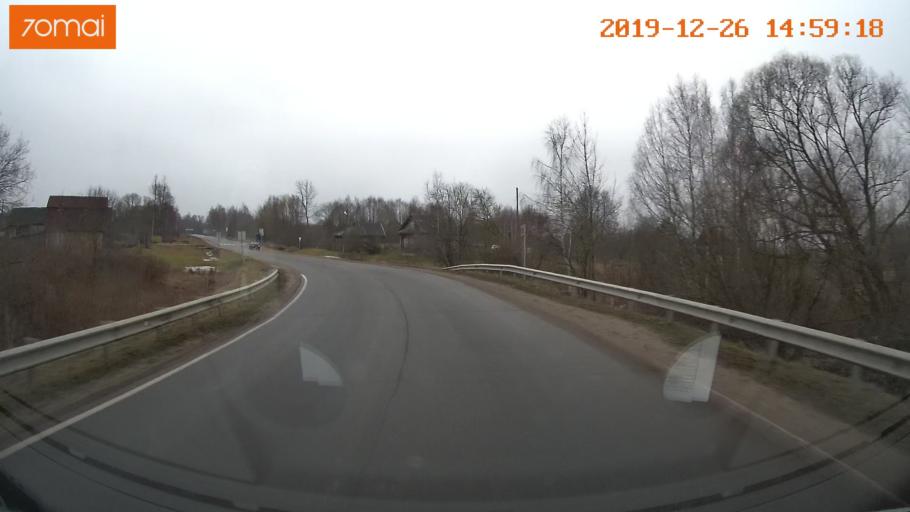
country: RU
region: Jaroslavl
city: Rybinsk
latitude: 58.2602
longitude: 38.8474
